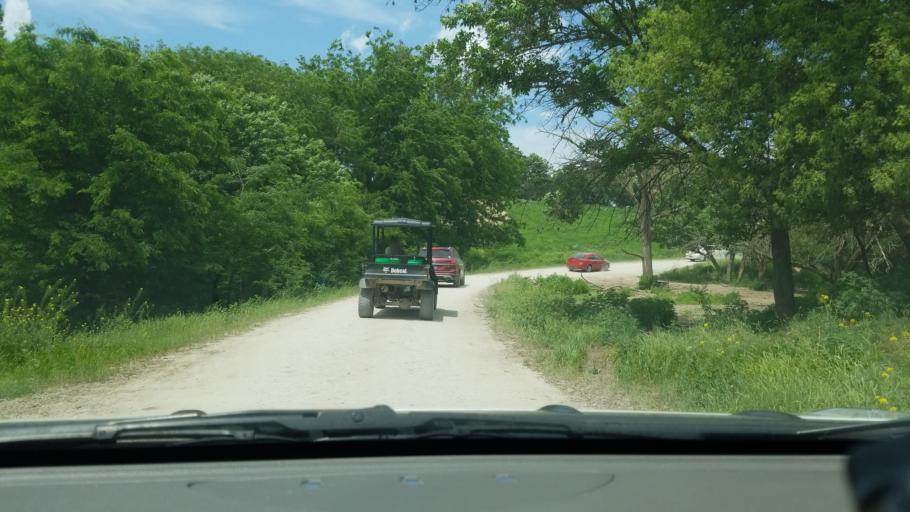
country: US
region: Nebraska
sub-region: Saunders County
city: Ashland
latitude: 41.0182
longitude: -96.2924
